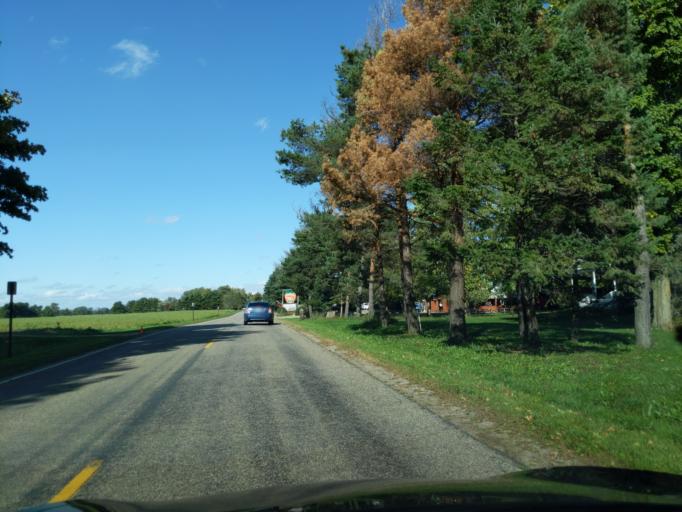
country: US
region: Michigan
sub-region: Eaton County
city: Potterville
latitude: 42.6348
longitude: -84.7977
